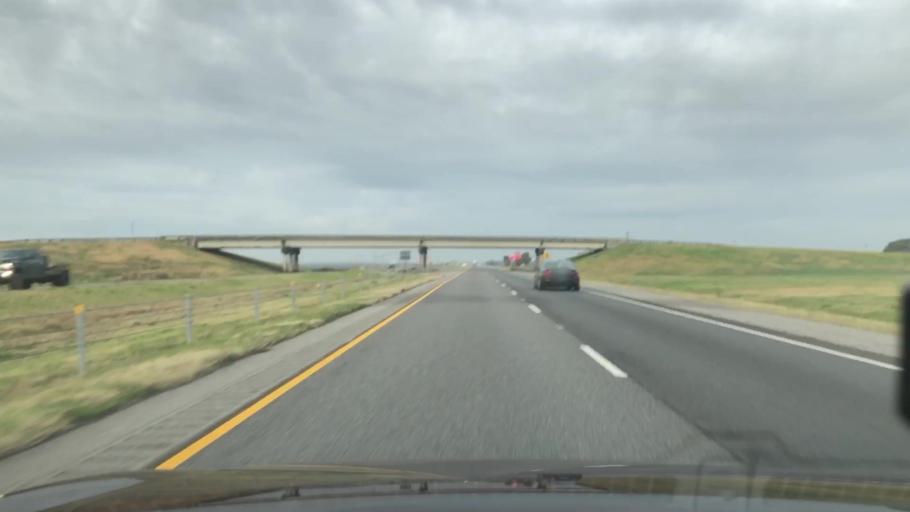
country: US
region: Mississippi
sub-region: Warren County
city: Vicksburg
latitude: 32.3250
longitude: -90.9547
